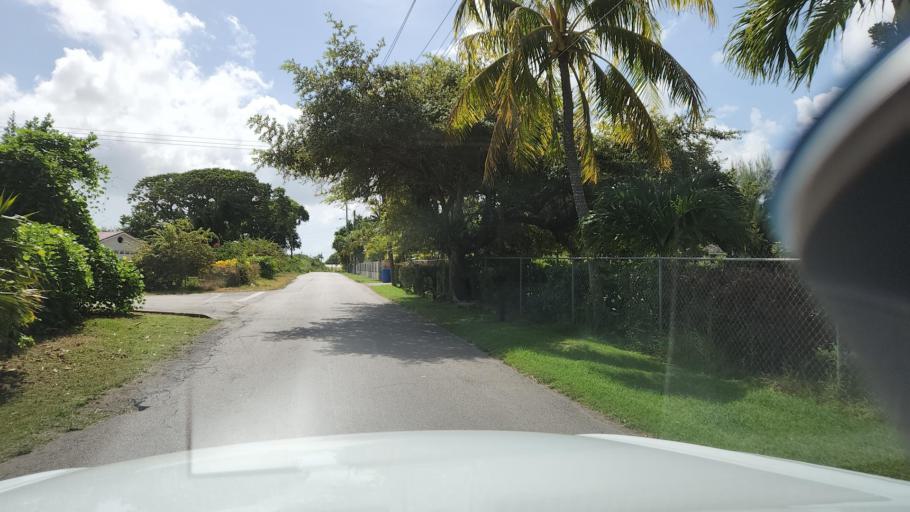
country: BB
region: Saint Philip
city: Crane
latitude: 13.1399
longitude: -59.4559
